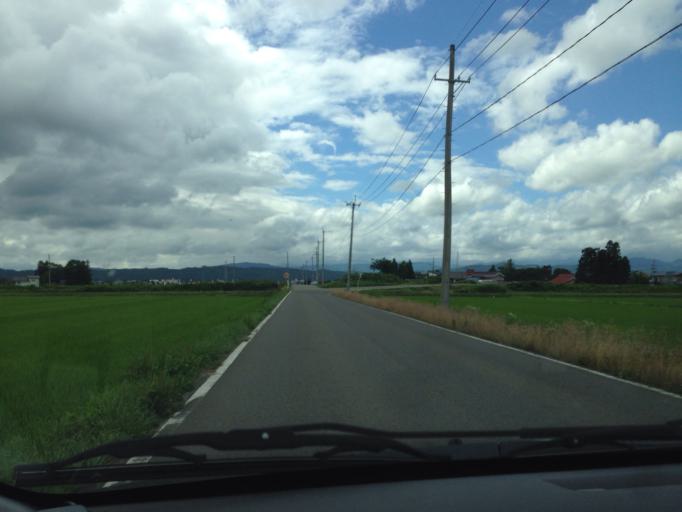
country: JP
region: Fukushima
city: Kitakata
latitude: 37.6376
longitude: 139.9011
